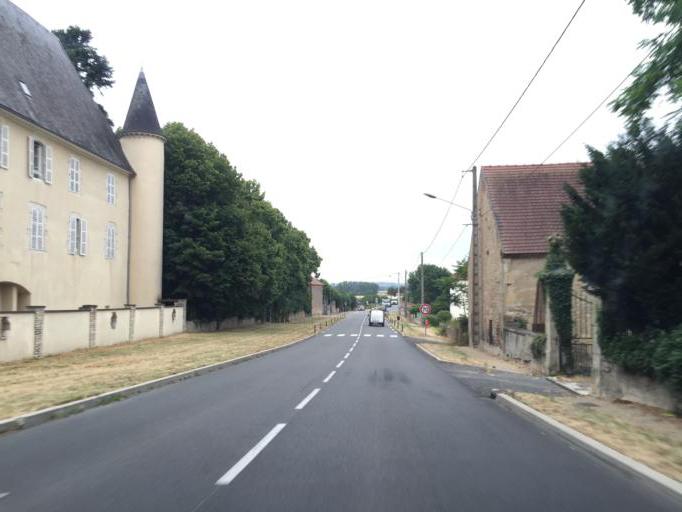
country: FR
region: Auvergne
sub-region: Departement de l'Allier
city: Brout-Vernet
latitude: 46.1640
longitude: 3.2372
